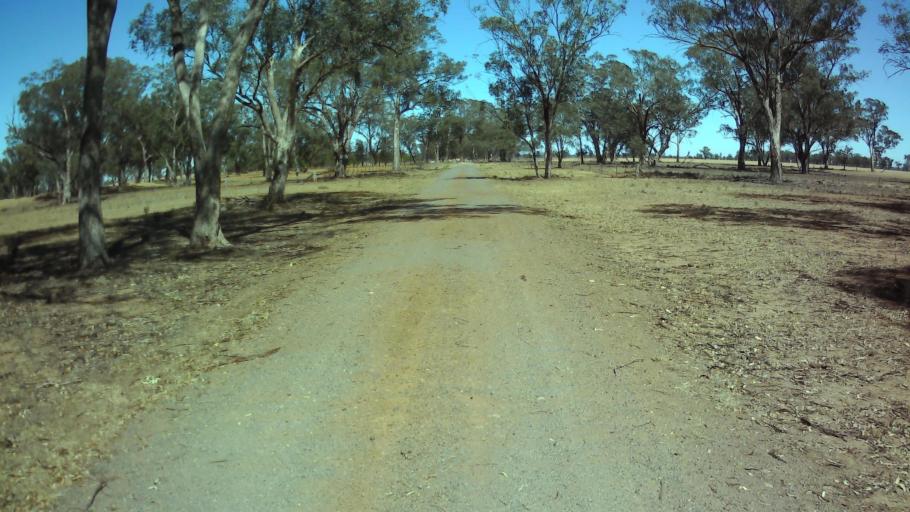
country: AU
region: New South Wales
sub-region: Weddin
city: Grenfell
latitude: -34.0920
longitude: 147.8860
